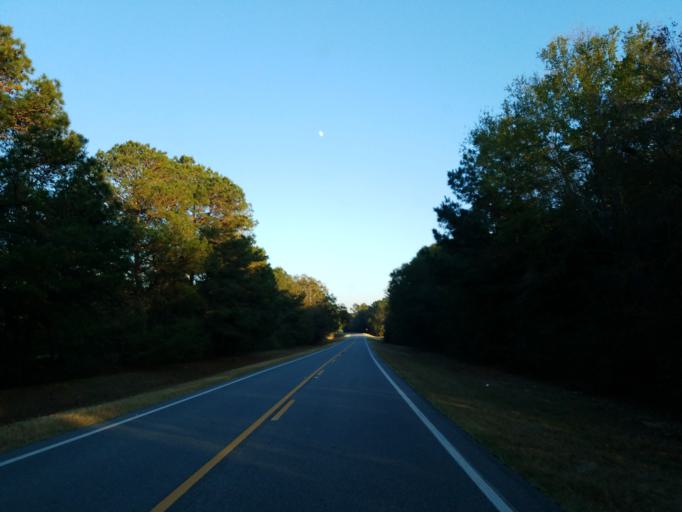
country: US
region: Georgia
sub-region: Wilcox County
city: Rochelle
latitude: 31.8150
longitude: -83.5080
